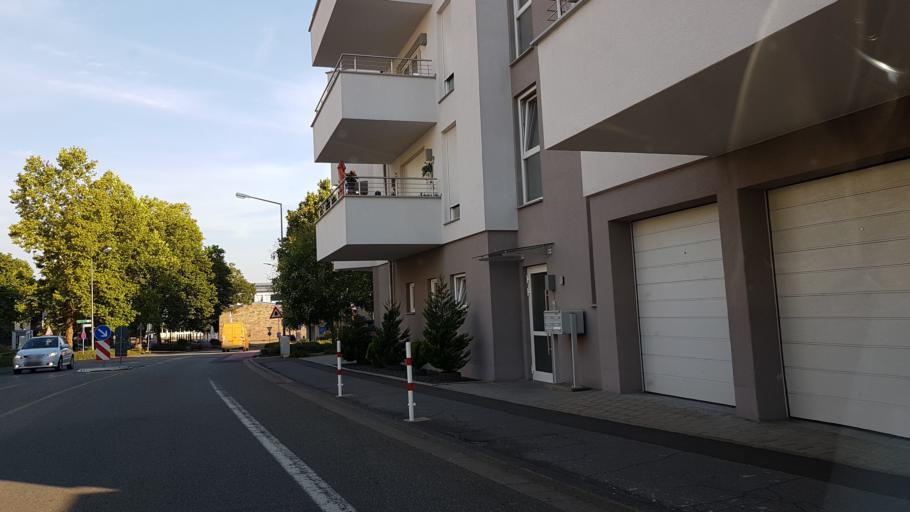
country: DE
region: Saarland
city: Homburg
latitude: 49.3193
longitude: 7.3371
